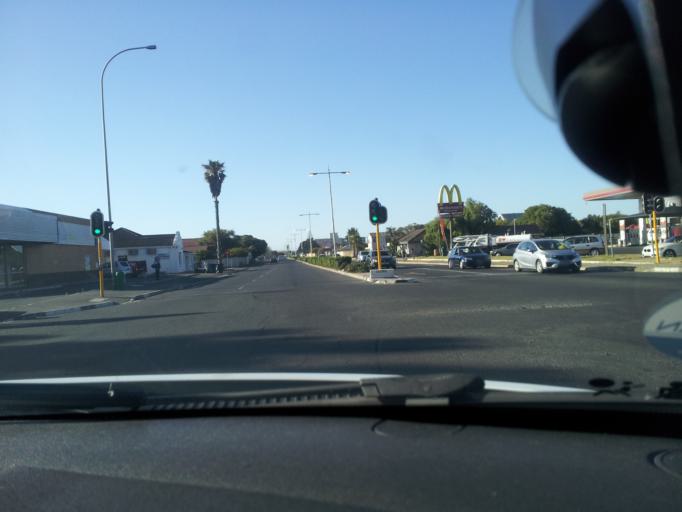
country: ZA
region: Western Cape
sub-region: Overberg District Municipality
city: Grabouw
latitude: -34.1217
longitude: 18.8357
